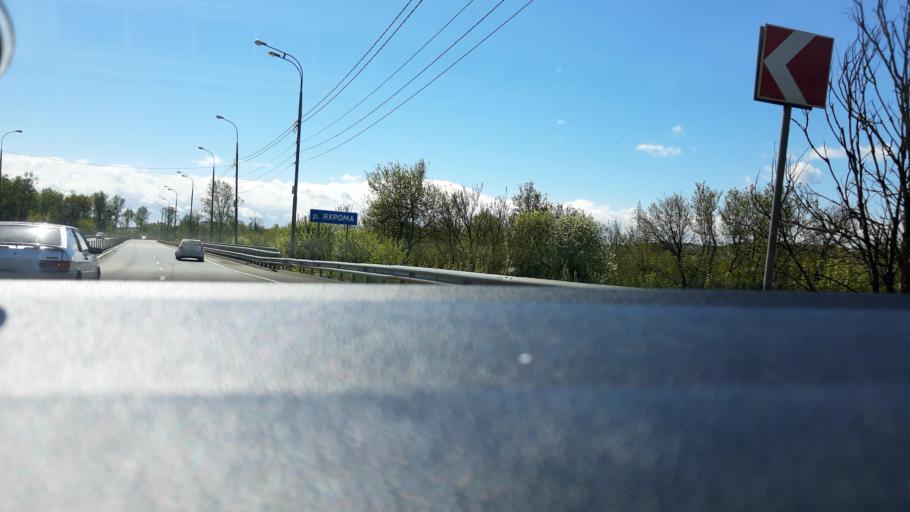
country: RU
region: Moskovskaya
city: Yakhroma
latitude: 56.2741
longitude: 37.5026
